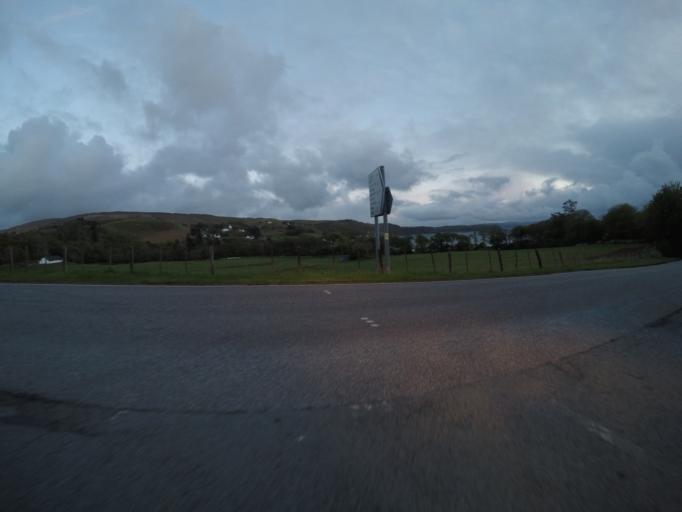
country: GB
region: Scotland
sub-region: Highland
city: Portree
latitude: 57.5920
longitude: -6.3591
